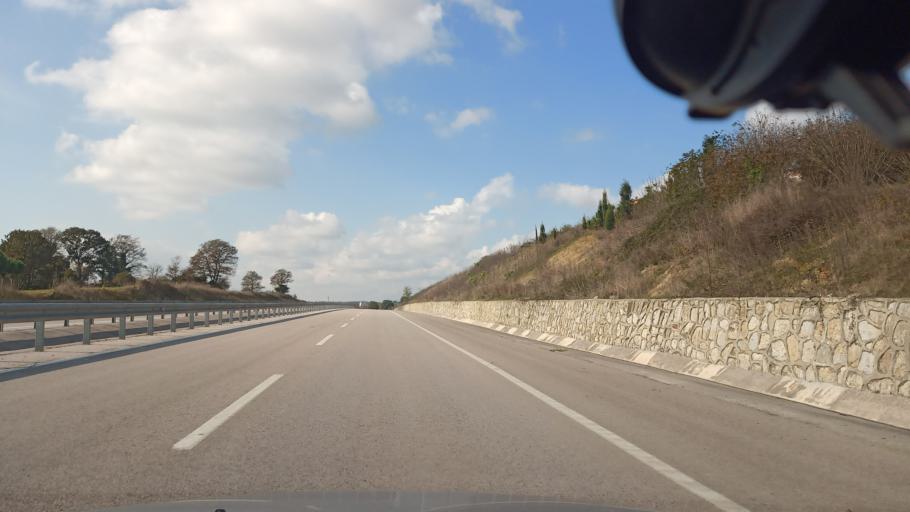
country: TR
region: Sakarya
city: Kaynarca
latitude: 41.0724
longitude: 30.3878
